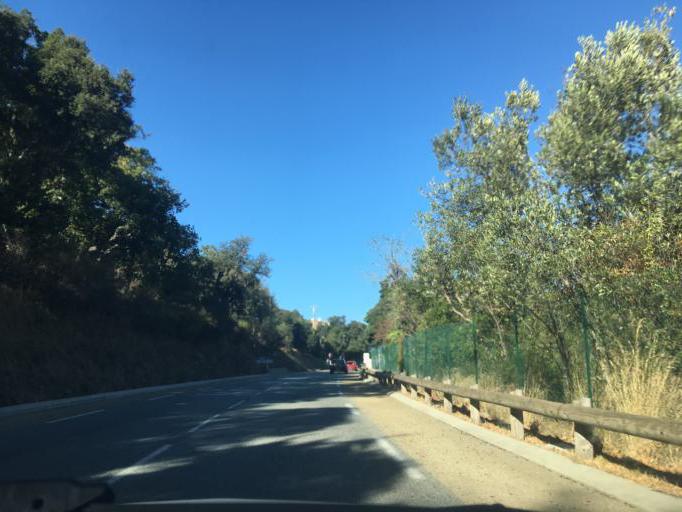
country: FR
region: Provence-Alpes-Cote d'Azur
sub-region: Departement du Var
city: La Garde-Freinet
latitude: 43.3111
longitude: 6.4706
